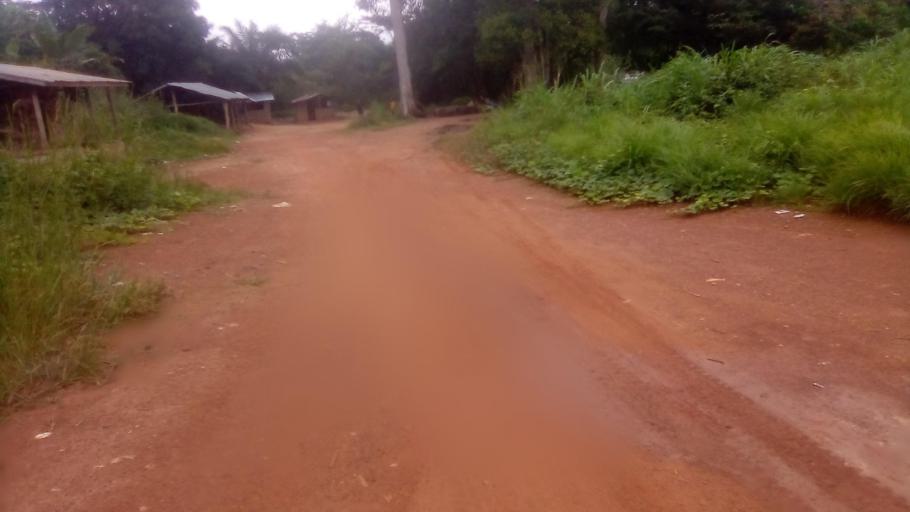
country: SL
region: Eastern Province
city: Kailahun
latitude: 8.3092
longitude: -10.5606
